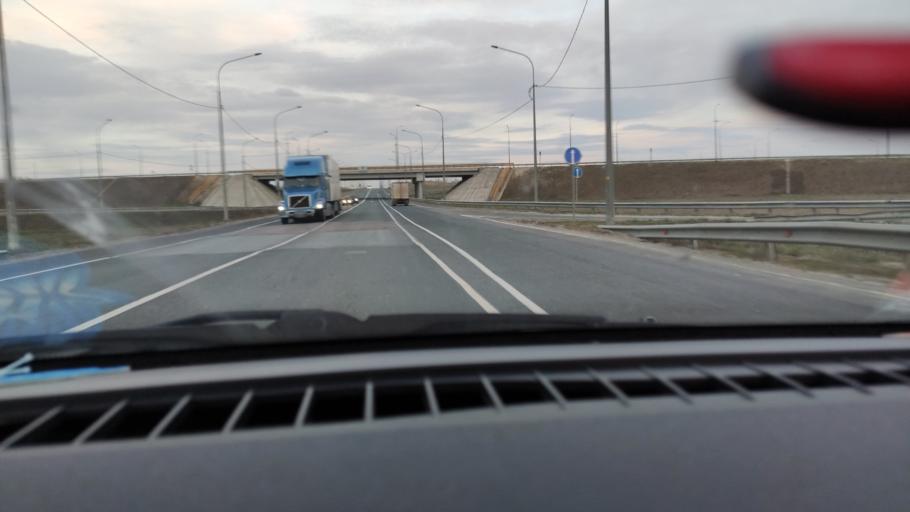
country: RU
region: Saratov
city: Yelshanka
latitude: 51.8305
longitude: 46.4266
